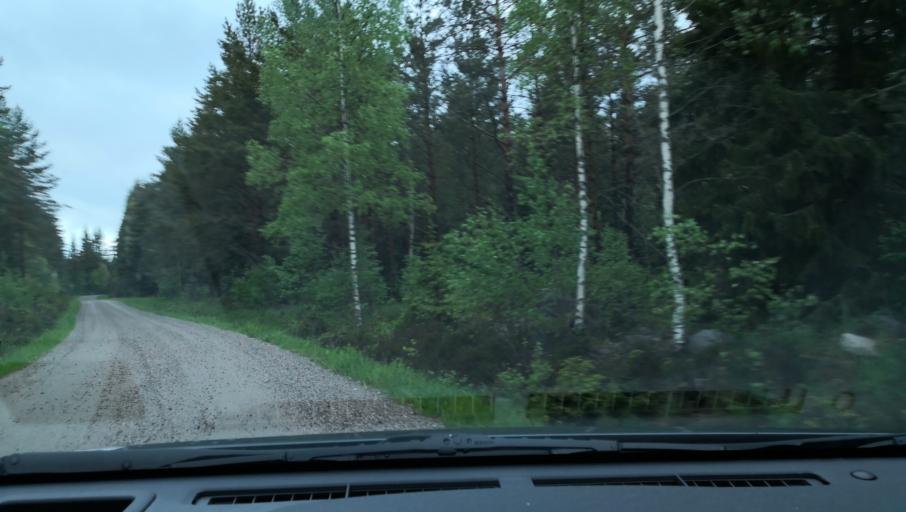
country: SE
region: Uppsala
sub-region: Heby Kommun
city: OEstervala
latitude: 59.9864
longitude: 17.2610
